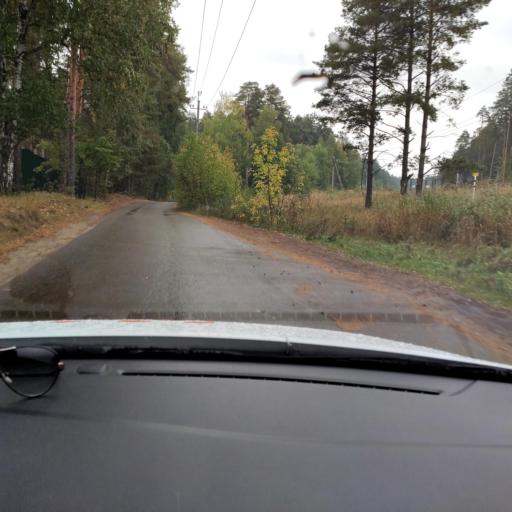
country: RU
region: Tatarstan
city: Verkhniy Uslon
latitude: 55.6416
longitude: 49.0189
